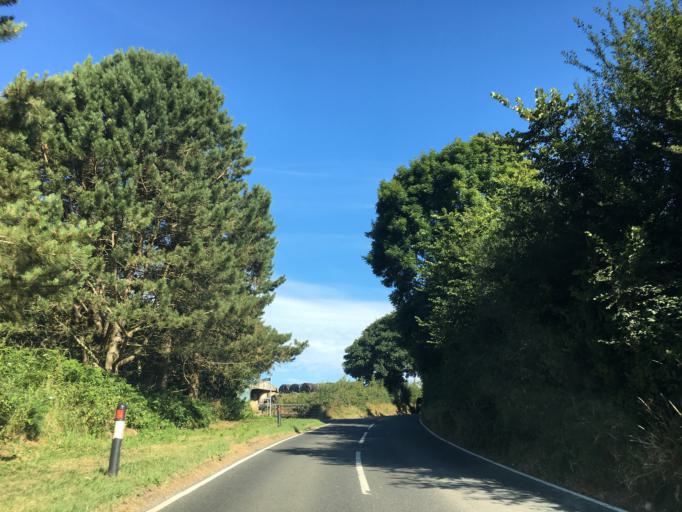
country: GB
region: England
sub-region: Isle of Wight
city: Niton
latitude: 50.6107
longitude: -1.2804
